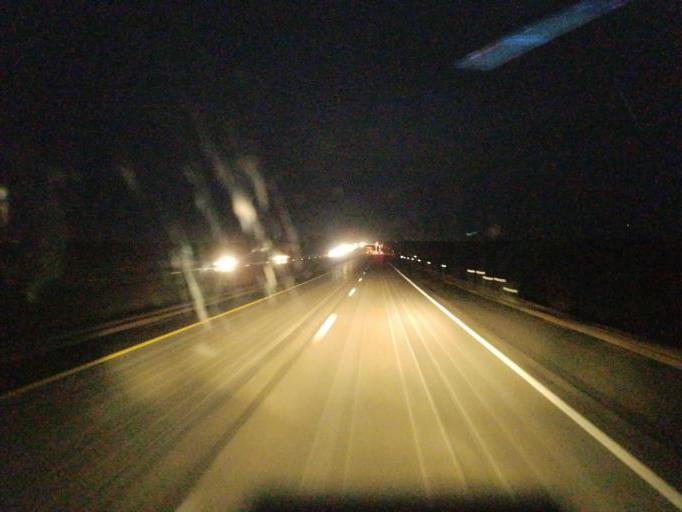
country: US
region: Iowa
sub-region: Guthrie County
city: Stuart
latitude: 41.4959
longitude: -94.3933
